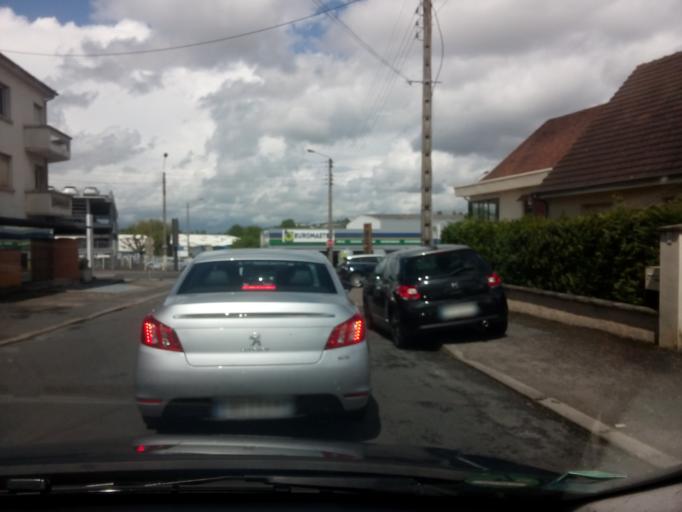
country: FR
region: Limousin
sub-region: Departement de la Correze
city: Brive-la-Gaillarde
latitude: 45.1498
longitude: 1.4967
